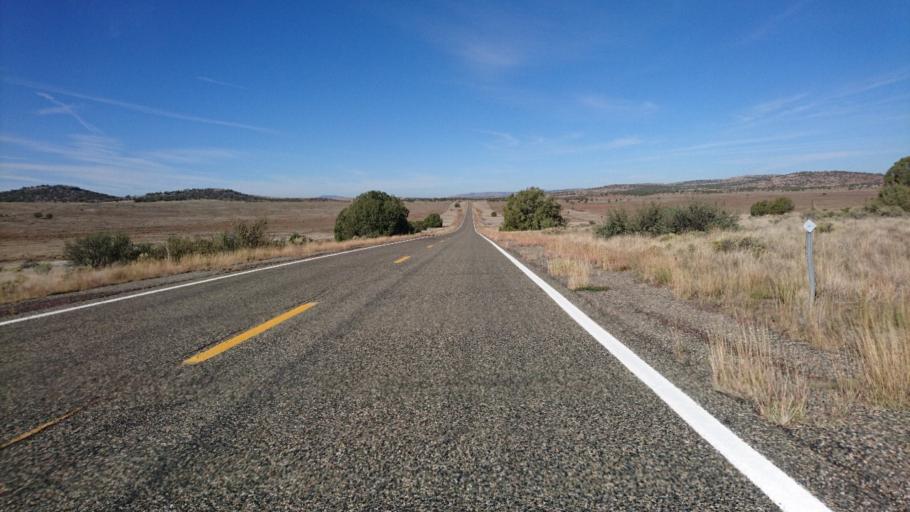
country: US
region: Arizona
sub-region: Yavapai County
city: Paulden
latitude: 35.2836
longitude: -112.7161
